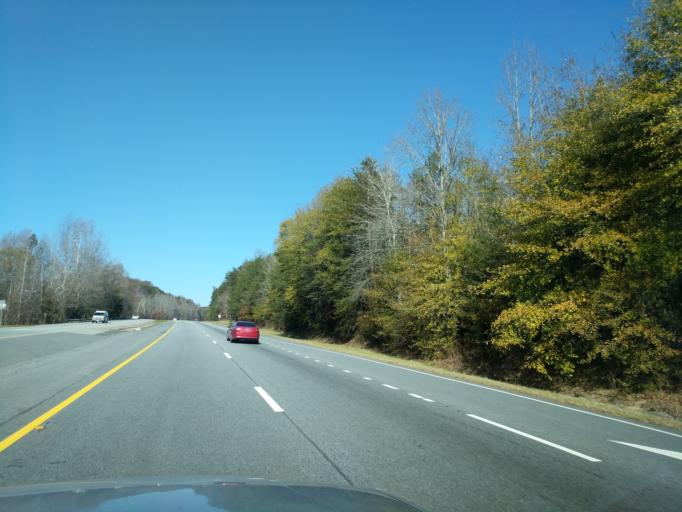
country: US
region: South Carolina
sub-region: Greenville County
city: Slater-Marietta
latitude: 35.0902
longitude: -82.4475
